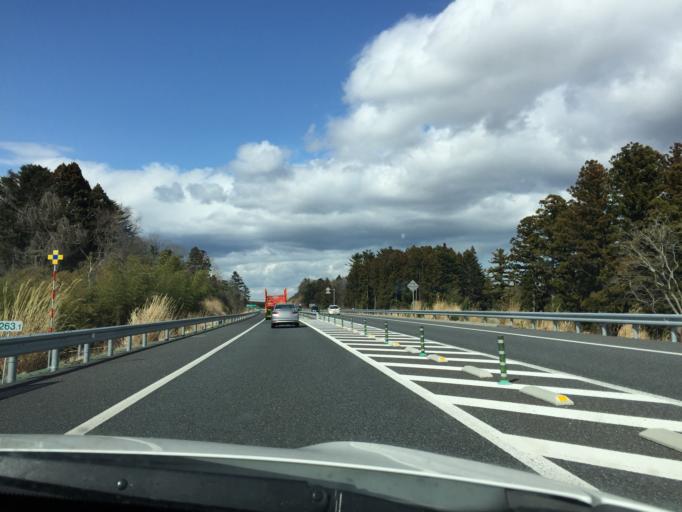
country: JP
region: Miyagi
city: Marumori
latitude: 37.7604
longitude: 140.9018
